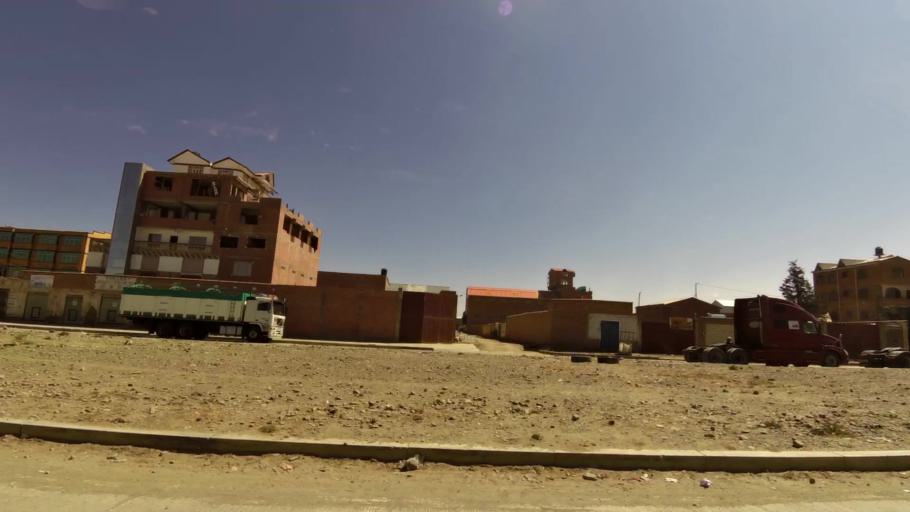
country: BO
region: La Paz
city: La Paz
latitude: -16.5480
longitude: -68.1814
